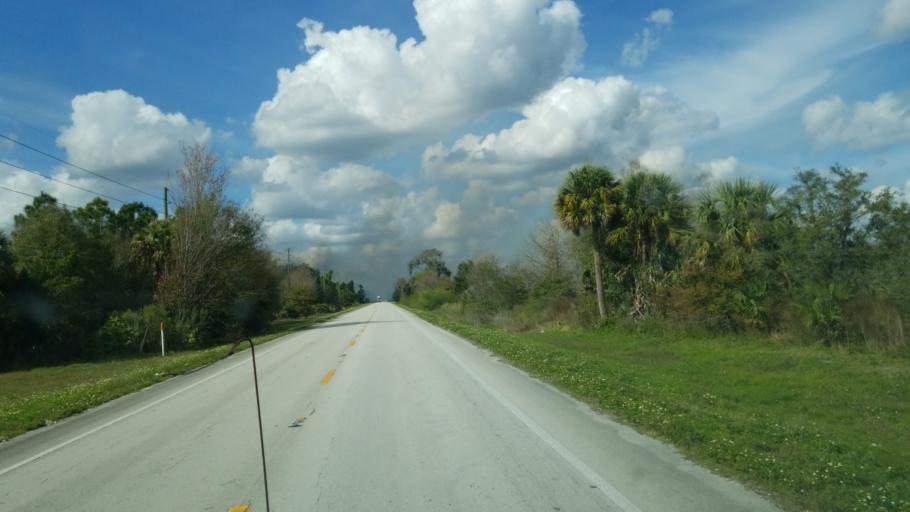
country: US
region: Florida
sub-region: Osceola County
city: Saint Cloud
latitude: 28.0411
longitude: -81.0472
